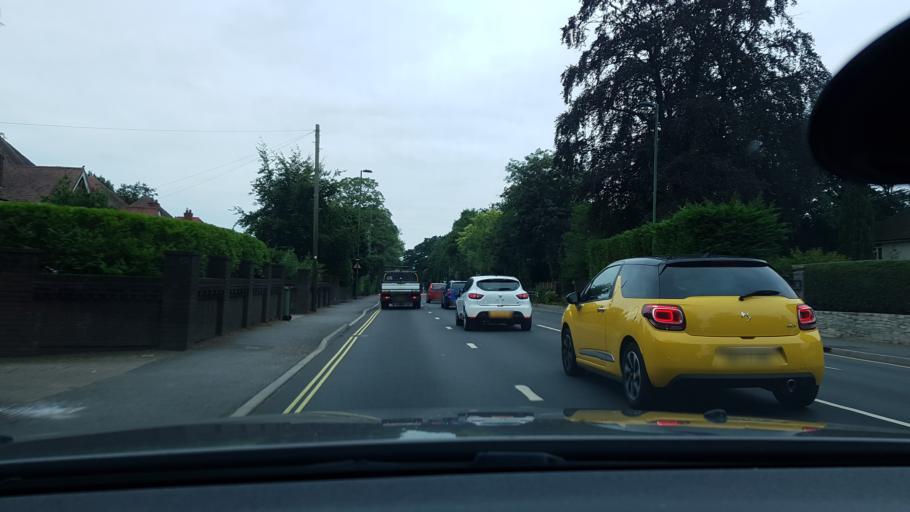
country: GB
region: England
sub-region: Southampton
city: Southampton
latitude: 50.9438
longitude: -1.4060
